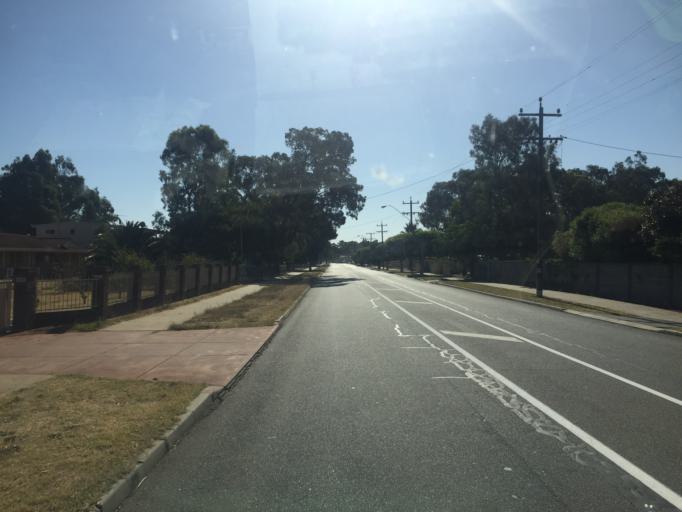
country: AU
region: Western Australia
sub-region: Gosnells
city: Kenwick
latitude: -32.0351
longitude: 115.9738
